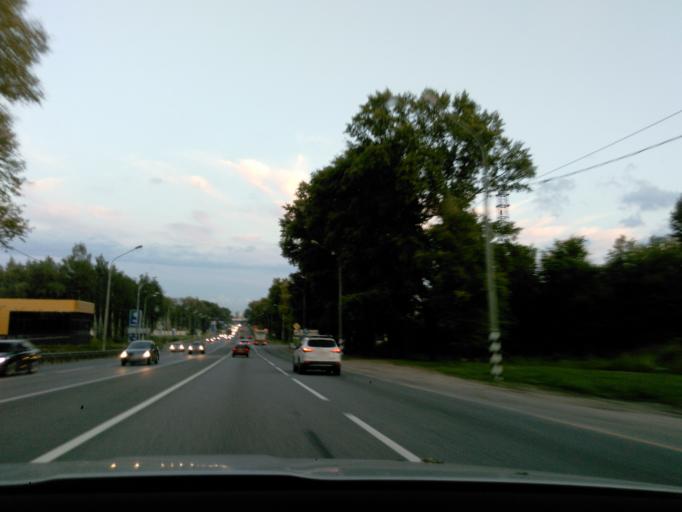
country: RU
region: Moskovskaya
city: Klin
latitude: 56.3486
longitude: 36.7058
